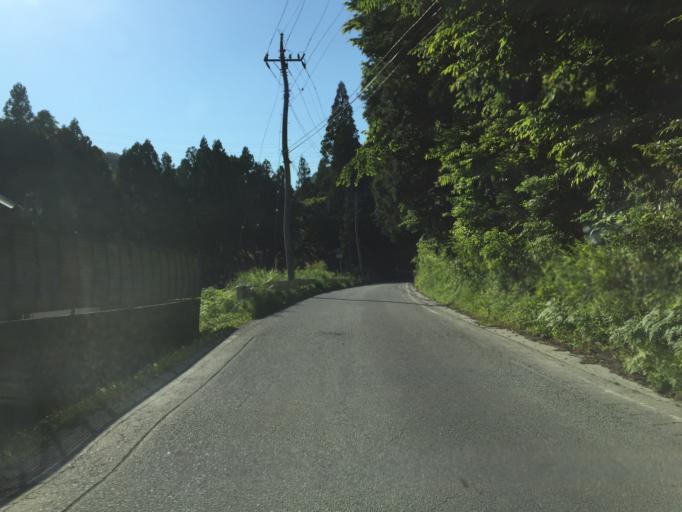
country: JP
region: Ibaraki
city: Kitaibaraki
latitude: 36.8634
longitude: 140.7153
